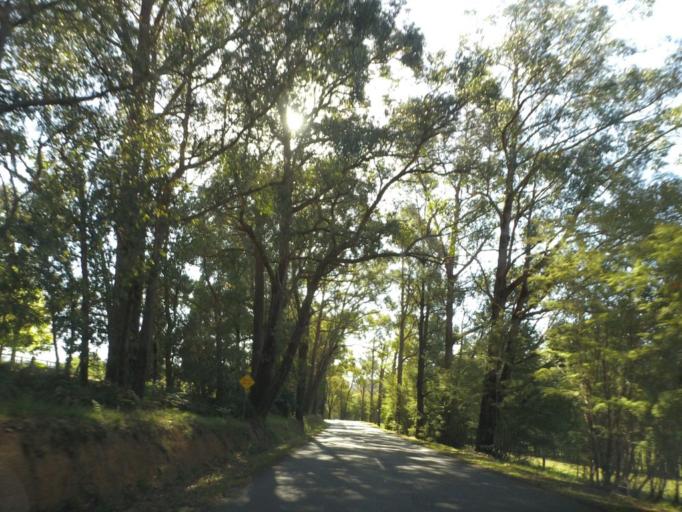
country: AU
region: Victoria
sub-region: Yarra Ranges
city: Yarra Junction
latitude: -37.8309
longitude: 145.6688
